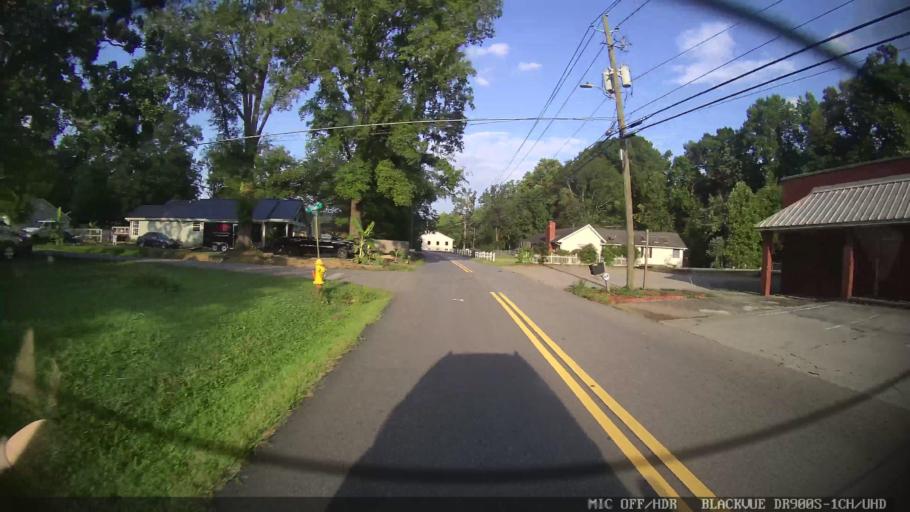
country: US
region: Georgia
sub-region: Bartow County
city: Rydal
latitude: 34.2798
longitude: -84.7466
